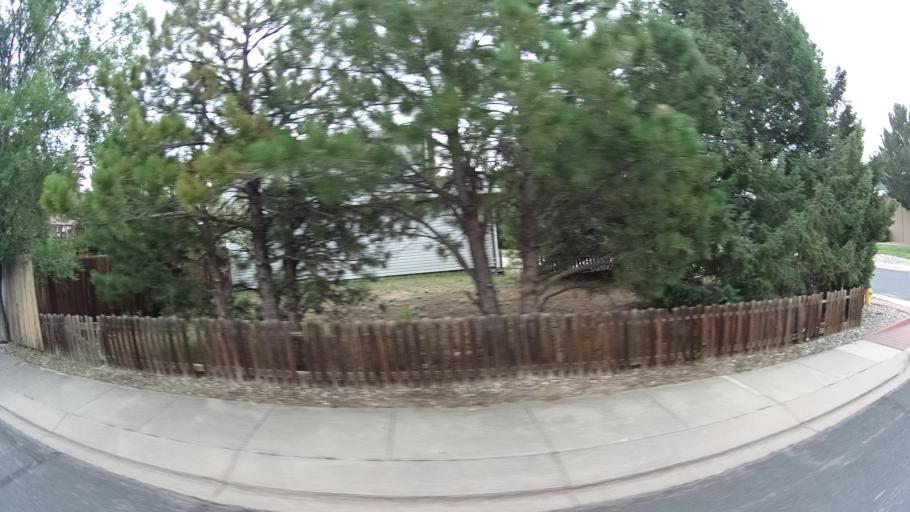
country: US
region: Colorado
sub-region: El Paso County
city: Colorado Springs
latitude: 38.9195
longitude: -104.8124
